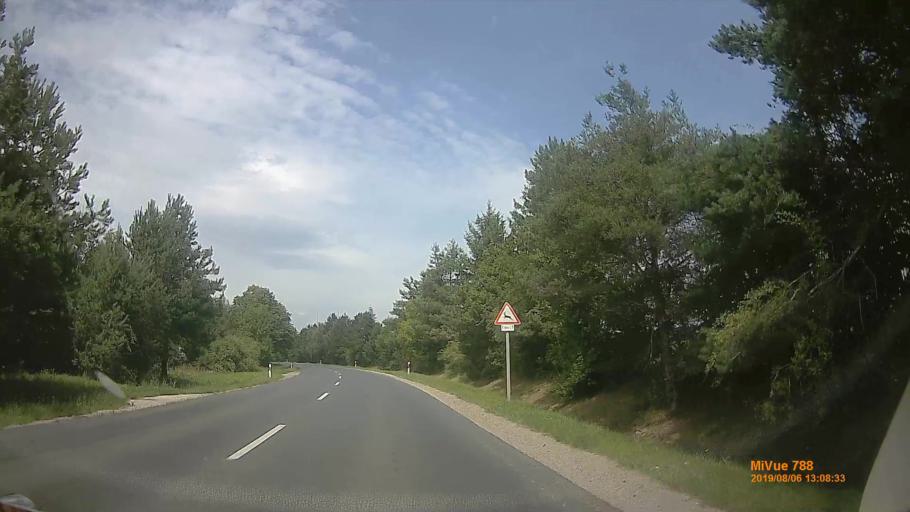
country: HU
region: Vas
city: Koszeg
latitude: 47.3902
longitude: 16.5546
